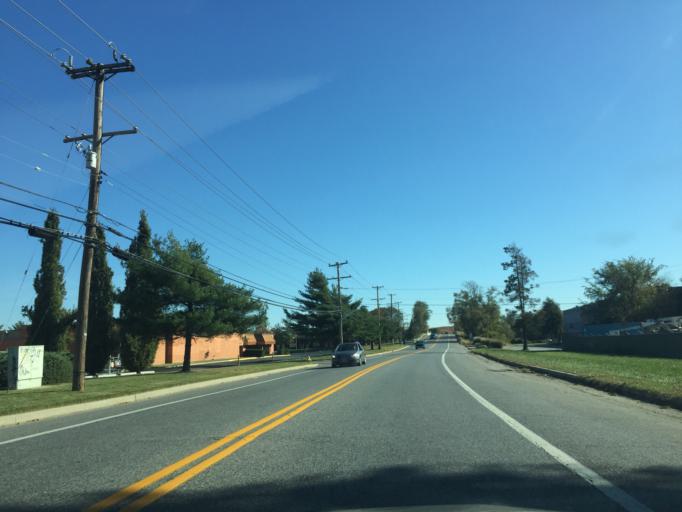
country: US
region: Maryland
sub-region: Anne Arundel County
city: Linthicum
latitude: 39.2241
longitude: -76.6565
